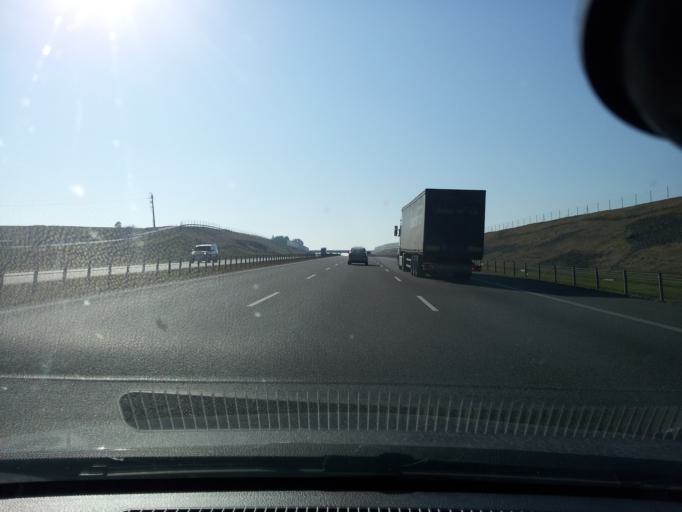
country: PL
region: Kujawsko-Pomorskie
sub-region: Powiat chelminski
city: Lisewo
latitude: 53.3883
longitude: 18.6862
